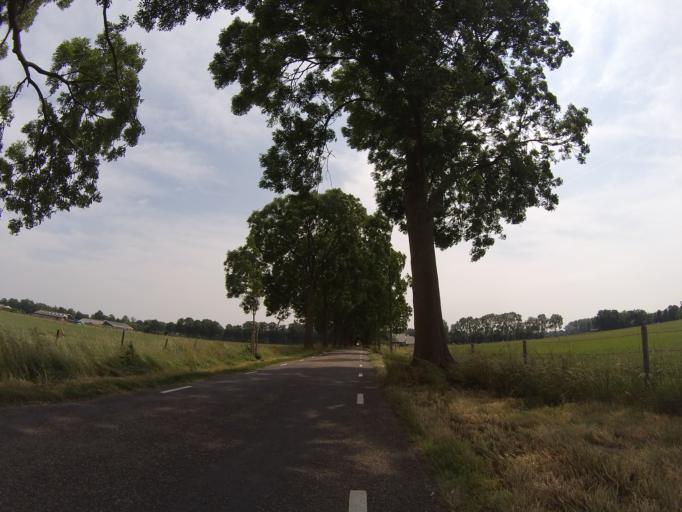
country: NL
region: Utrecht
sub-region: Gemeente Zeist
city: Zeist
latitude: 52.0674
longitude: 5.2346
